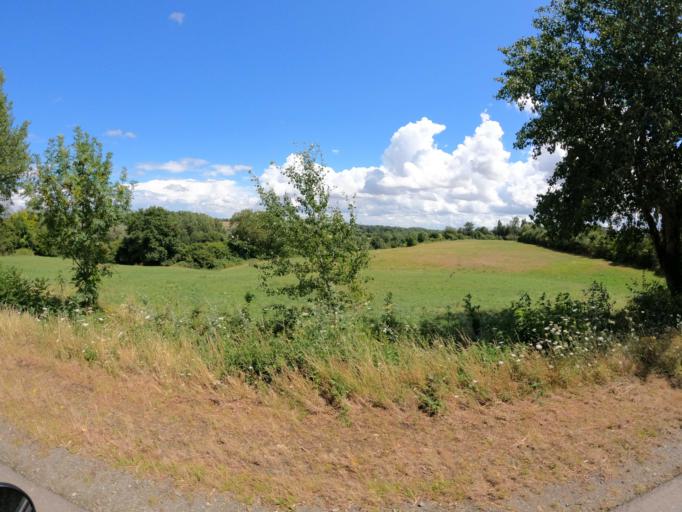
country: FR
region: Pays de la Loire
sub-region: Departement de la Sarthe
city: Brulon
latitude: 47.9431
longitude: -0.2551
